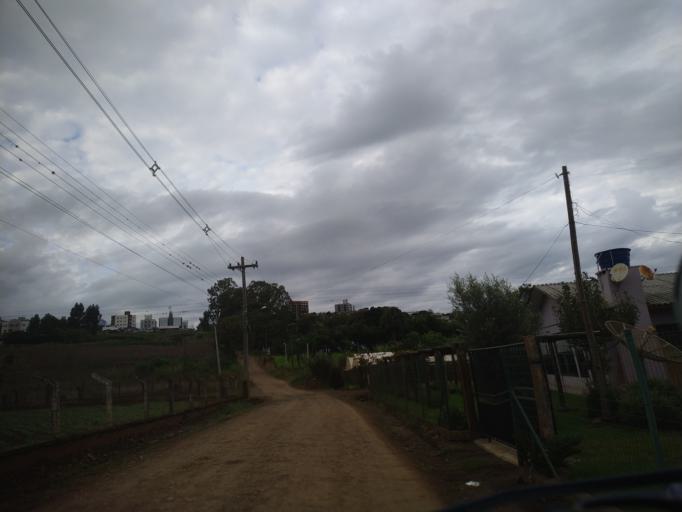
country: BR
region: Santa Catarina
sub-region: Chapeco
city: Chapeco
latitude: -27.0658
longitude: -52.6125
